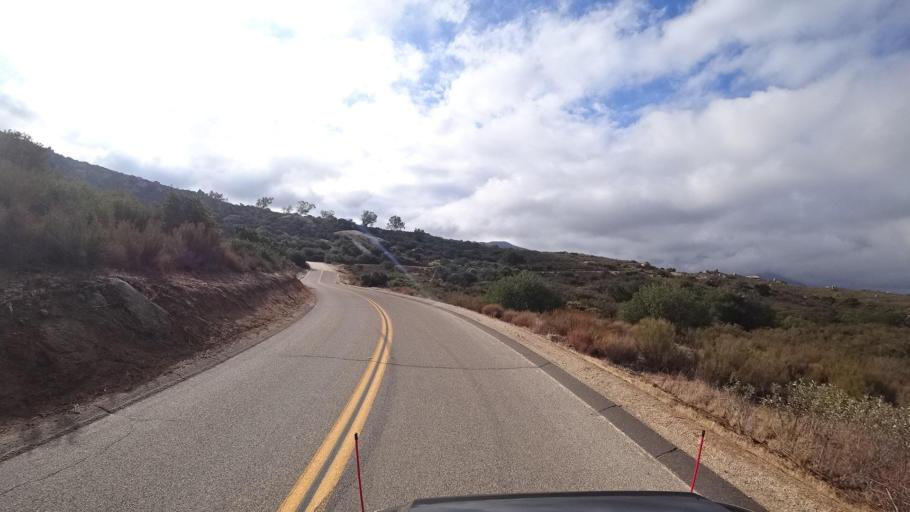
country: MX
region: Baja California
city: Tecate
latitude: 32.6439
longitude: -116.6360
